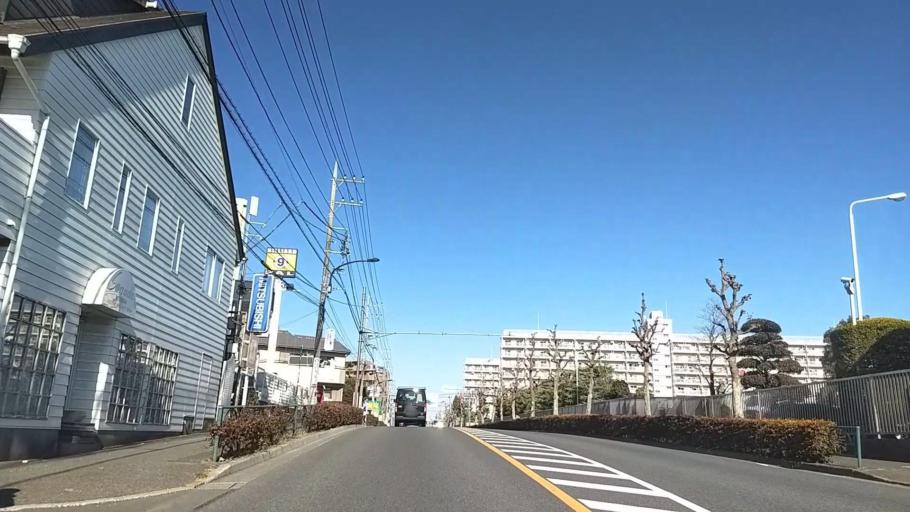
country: JP
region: Tokyo
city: Hachioji
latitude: 35.6361
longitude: 139.2877
